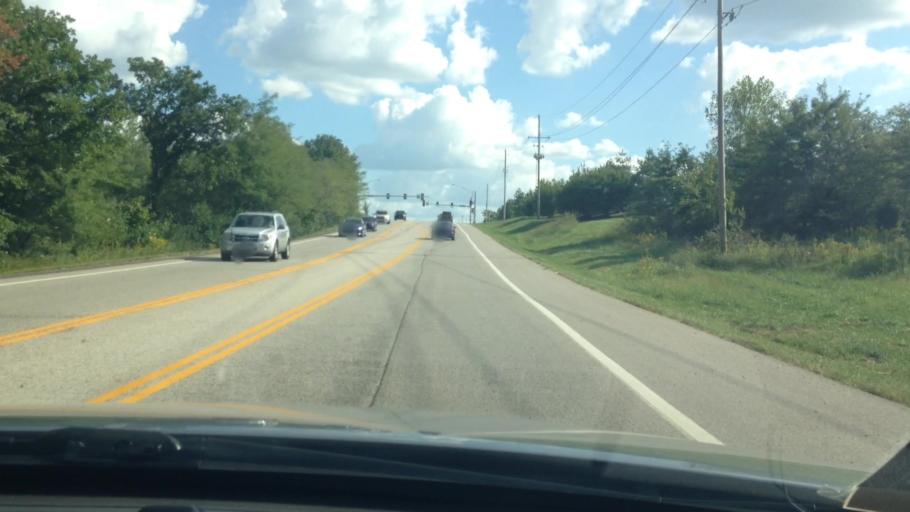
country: US
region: Missouri
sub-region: Clay County
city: Liberty
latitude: 39.2809
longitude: -94.4673
